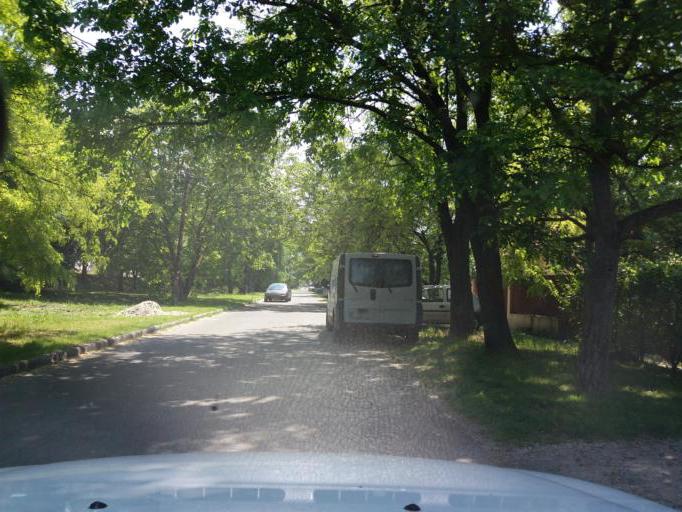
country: HU
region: Budapest
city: Budapest XXII. keruelet
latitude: 47.4454
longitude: 19.0305
